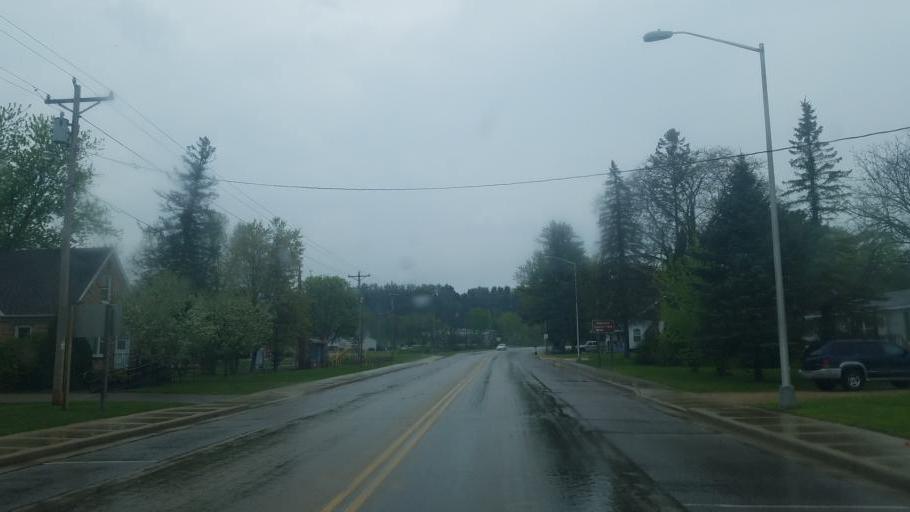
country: US
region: Wisconsin
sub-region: Sauk County
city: Reedsburg
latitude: 43.5831
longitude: -90.1297
